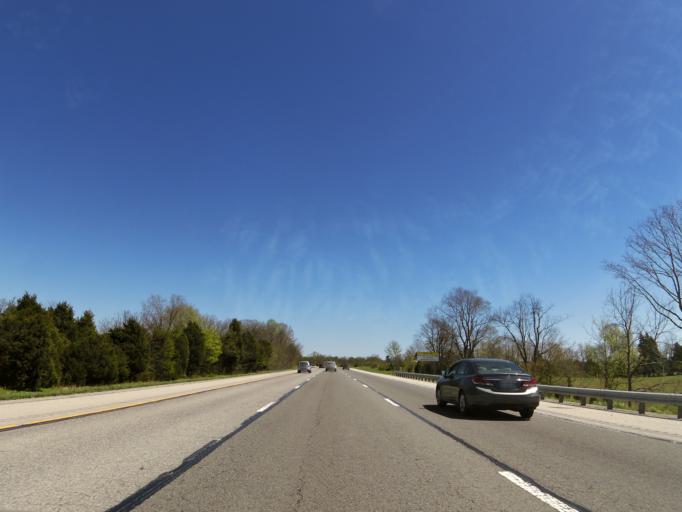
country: US
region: Kentucky
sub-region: Warren County
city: Bowling Green
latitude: 37.0122
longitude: -86.2989
